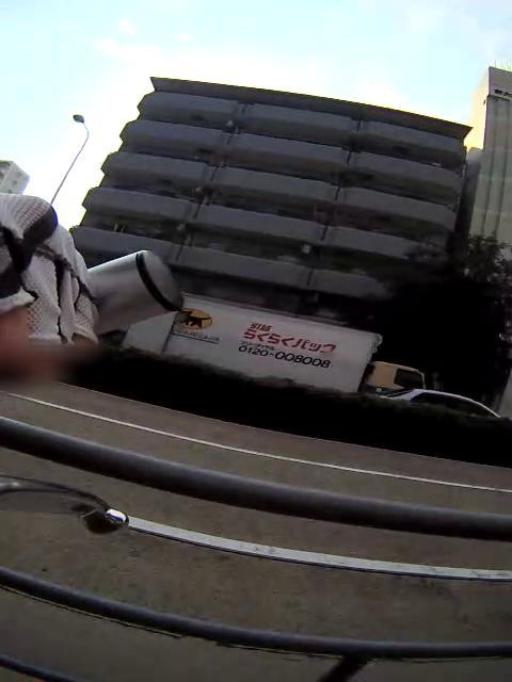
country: JP
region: Osaka
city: Suita
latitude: 34.7334
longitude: 135.4865
